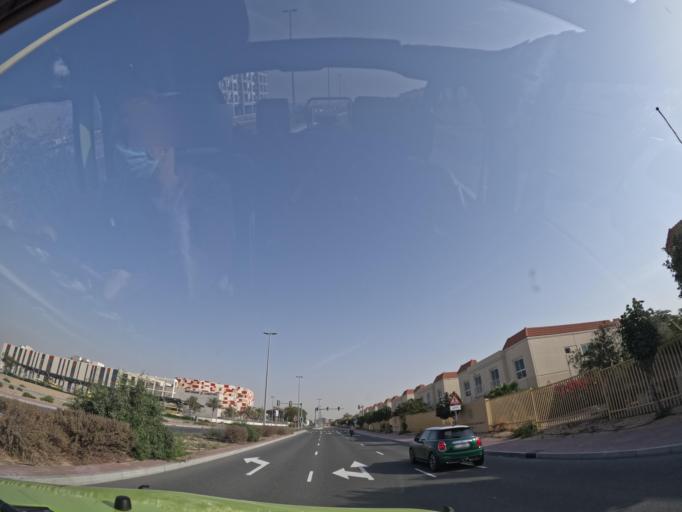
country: AE
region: Dubai
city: Dubai
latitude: 25.1266
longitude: 55.3560
